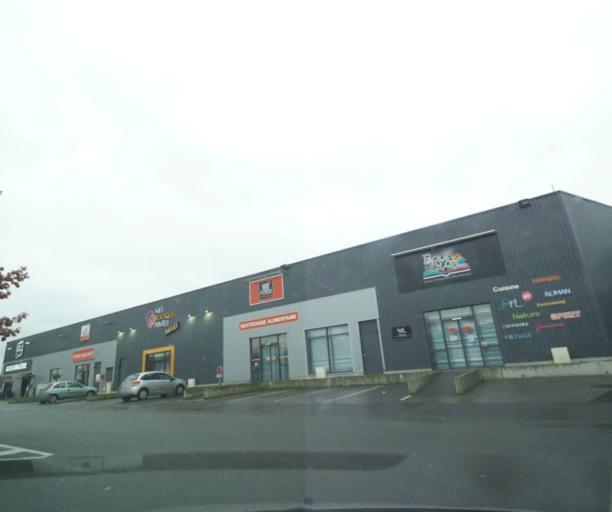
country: FR
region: Nord-Pas-de-Calais
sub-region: Departement du Nord
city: Herin
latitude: 50.3378
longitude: 3.4618
